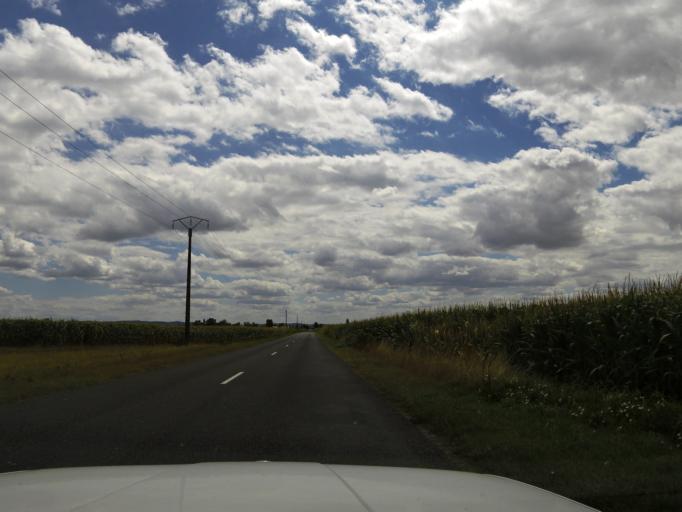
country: FR
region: Rhone-Alpes
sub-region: Departement de l'Ain
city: Saint-Maurice-de-Gourdans
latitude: 45.8050
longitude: 5.2131
